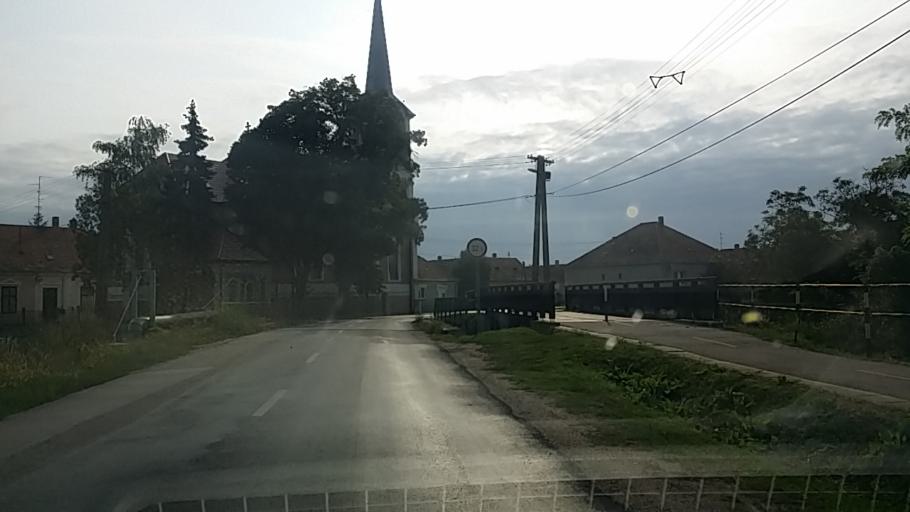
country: HU
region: Gyor-Moson-Sopron
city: Fertoszentmiklos
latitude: 47.6070
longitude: 16.9044
